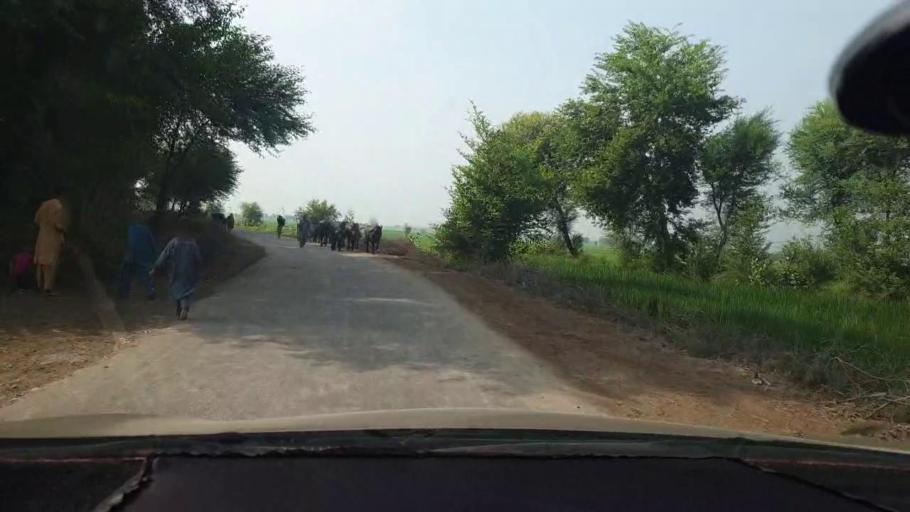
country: PK
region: Sindh
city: Goth Garelo
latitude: 27.4910
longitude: 68.0102
